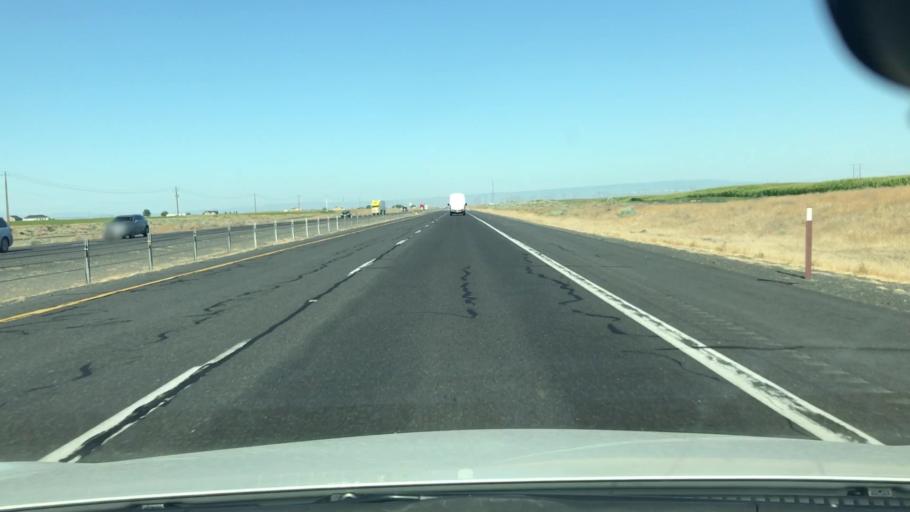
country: US
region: Washington
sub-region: Grant County
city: Cascade Valley
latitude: 47.1042
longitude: -119.5001
